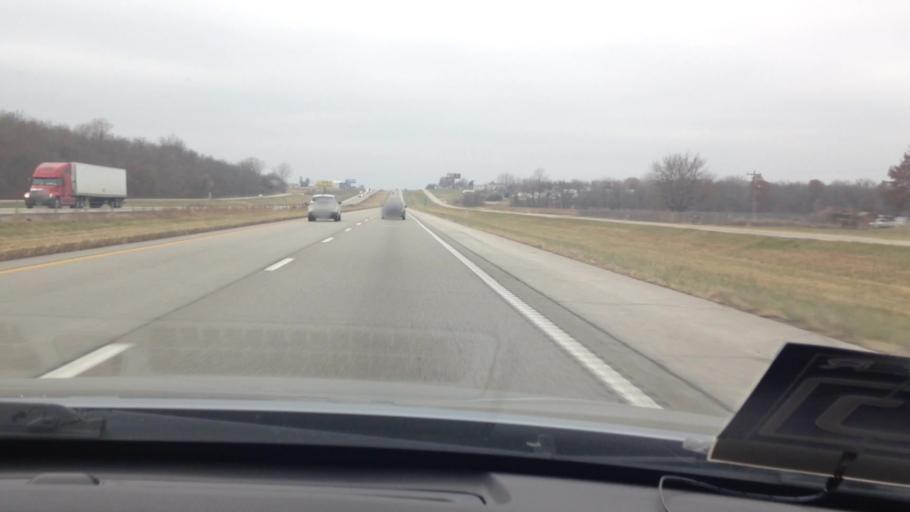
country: US
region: Missouri
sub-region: Cass County
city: Peculiar
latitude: 38.7000
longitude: -94.4331
